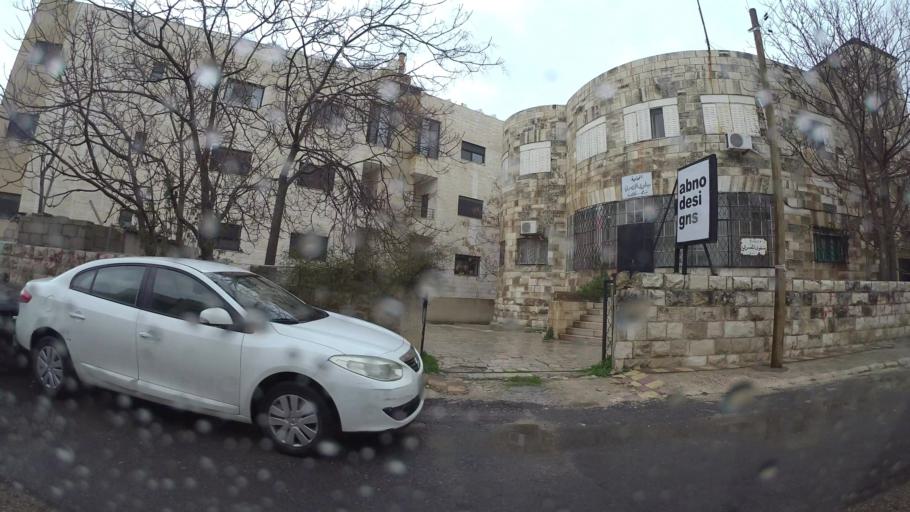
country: JO
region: Amman
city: Amman
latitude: 31.9571
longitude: 35.9275
